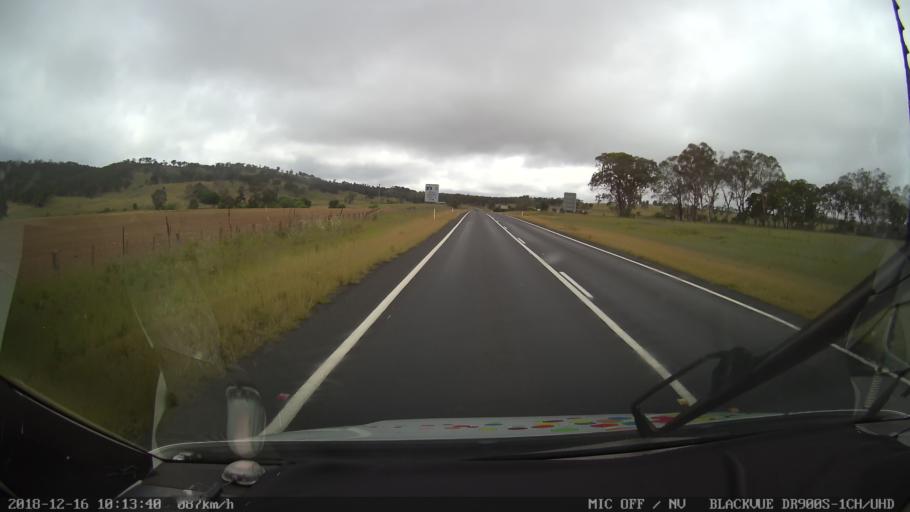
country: AU
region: New South Wales
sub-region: Glen Innes Severn
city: Glen Innes
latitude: -29.2949
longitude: 151.9555
